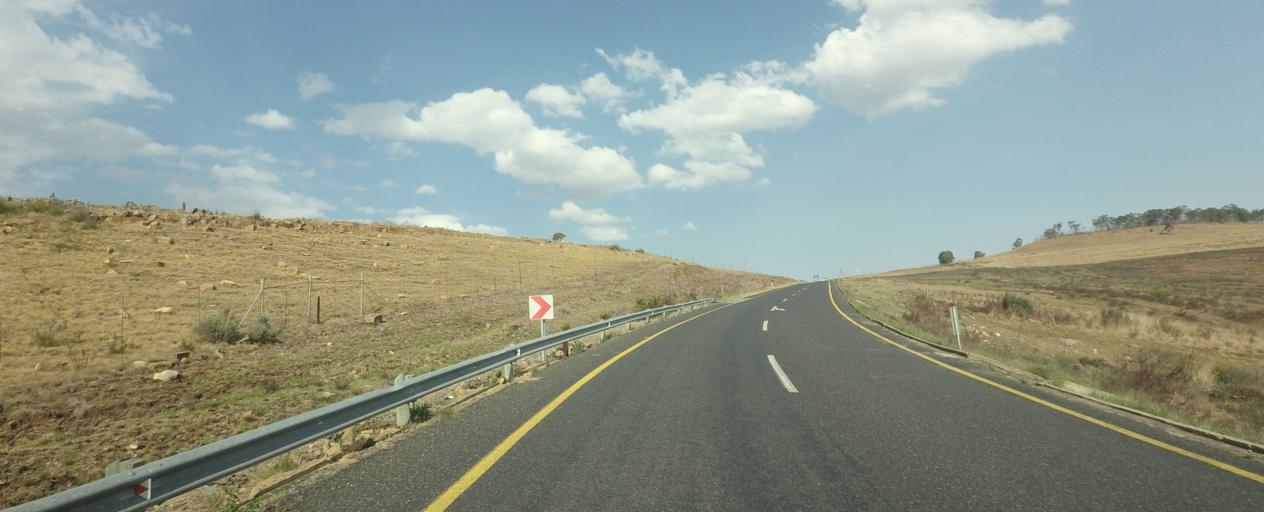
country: ZA
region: Mpumalanga
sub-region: Ehlanzeni District
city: Lydenburg
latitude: -25.1039
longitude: 30.5707
